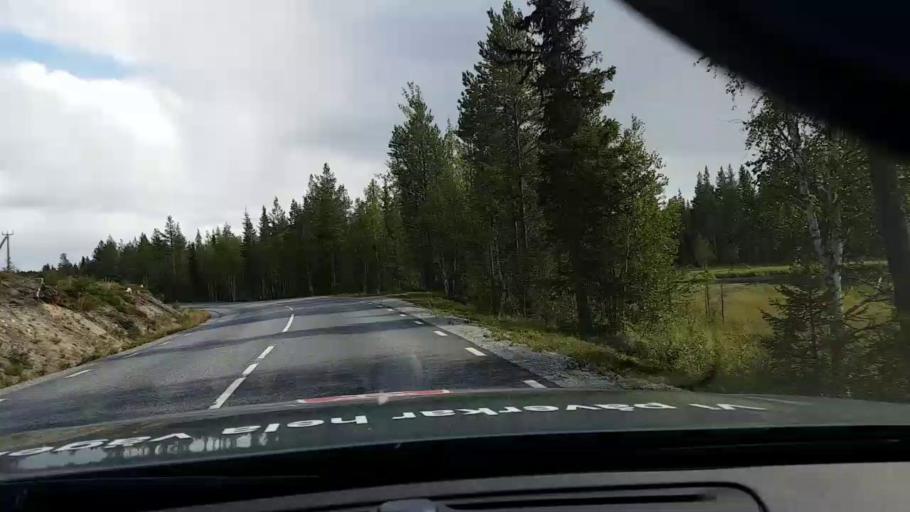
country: SE
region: Vaesterbotten
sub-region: Asele Kommun
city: Asele
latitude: 63.8487
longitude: 17.4037
